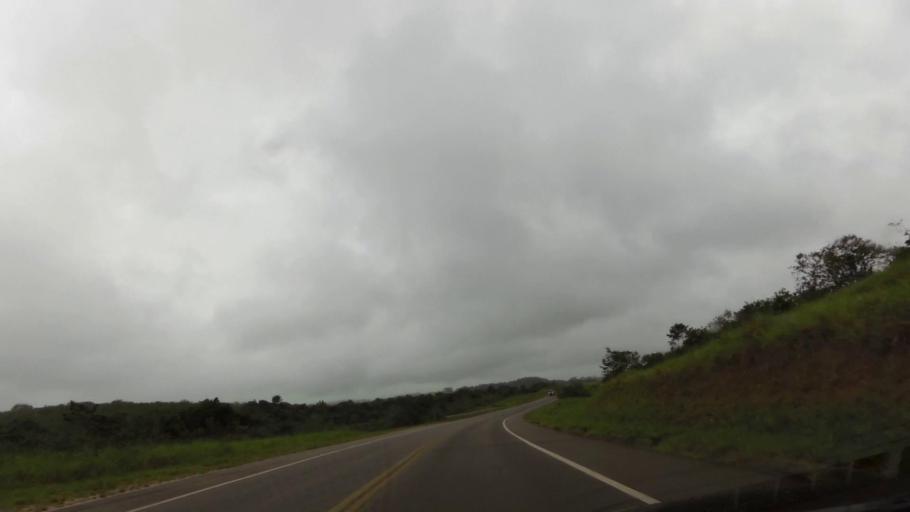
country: BR
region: Espirito Santo
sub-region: Guarapari
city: Guarapari
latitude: -20.7172
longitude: -40.5761
